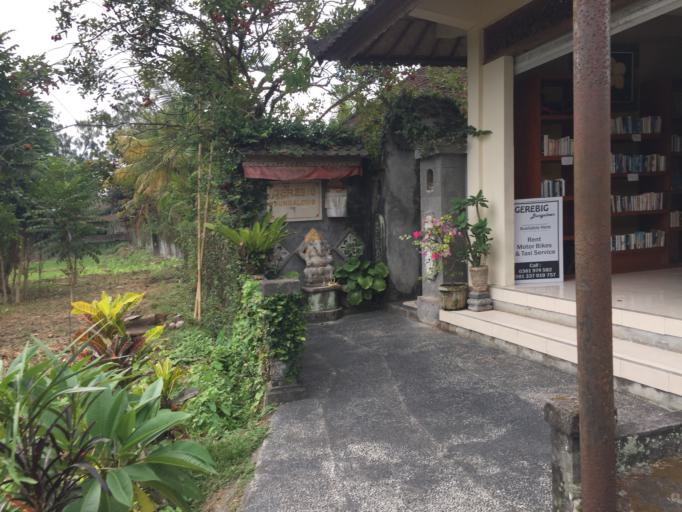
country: ID
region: Bali
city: Banjar Pande
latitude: -8.5056
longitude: 115.2518
